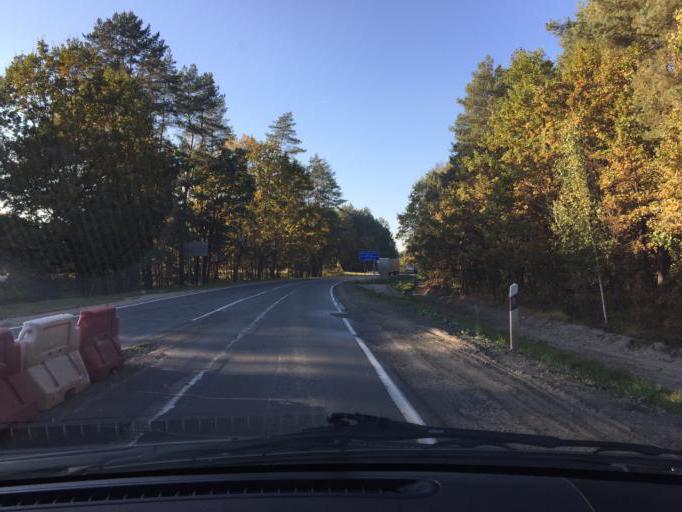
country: BY
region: Brest
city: Luninyets
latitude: 52.2796
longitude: 26.8328
